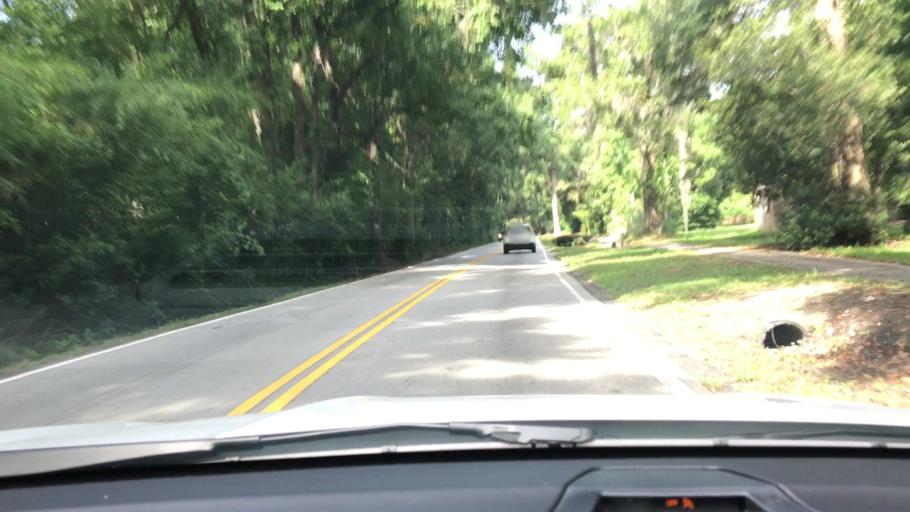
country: US
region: South Carolina
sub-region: Charleston County
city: Mount Pleasant
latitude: 32.8439
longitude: -79.8362
